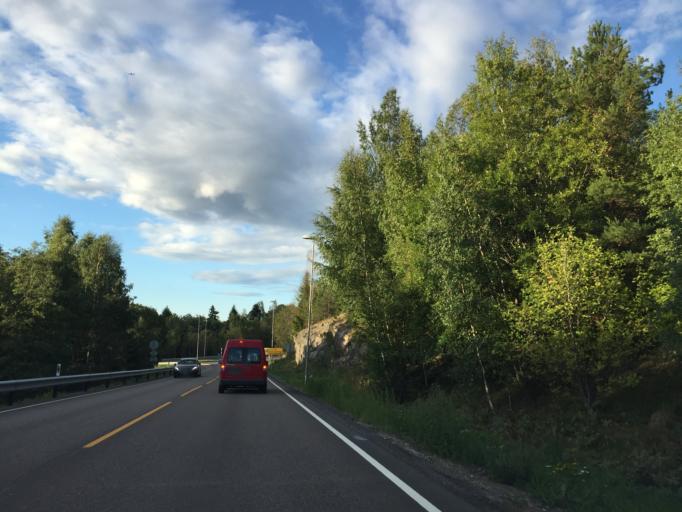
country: NO
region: Akershus
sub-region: Fet
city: Fetsund
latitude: 59.9209
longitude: 11.1836
